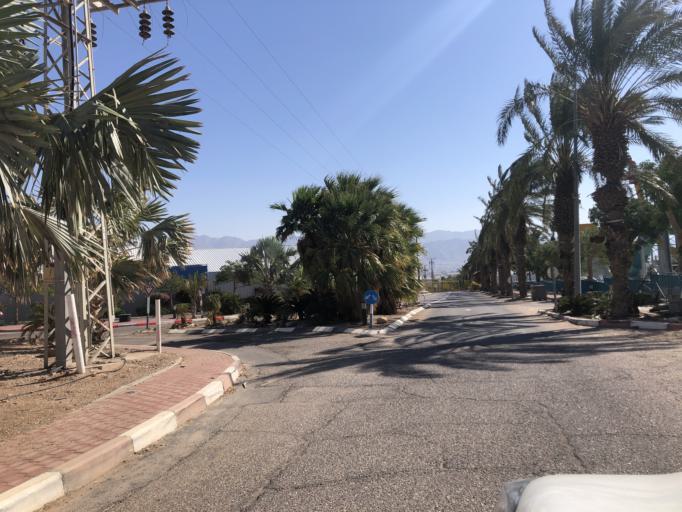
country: IL
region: Southern District
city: Eilat
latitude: 29.5810
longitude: 34.9635
